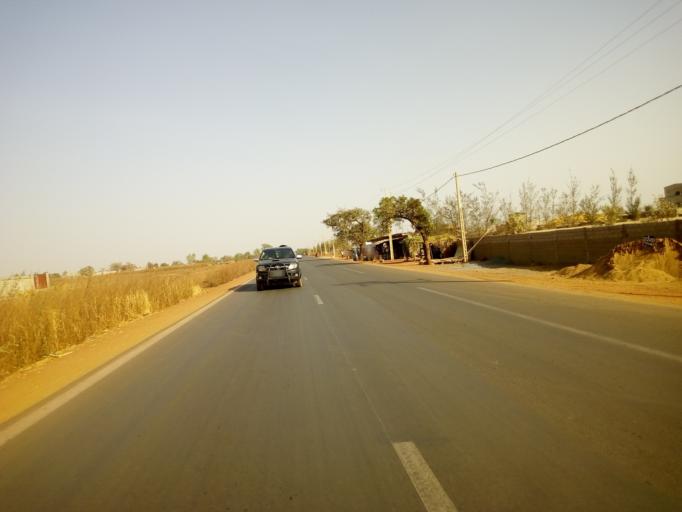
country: ML
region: Bamako
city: Bamako
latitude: 12.5836
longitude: -7.8219
